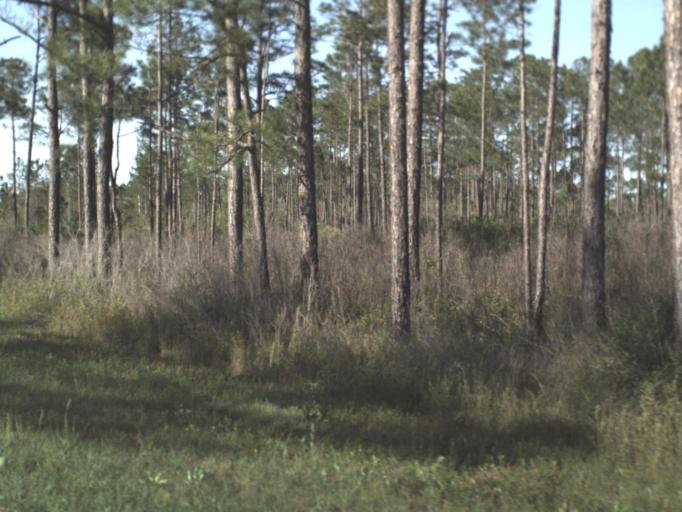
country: US
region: Florida
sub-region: Gulf County
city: Wewahitchka
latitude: 30.0880
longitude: -84.9838
